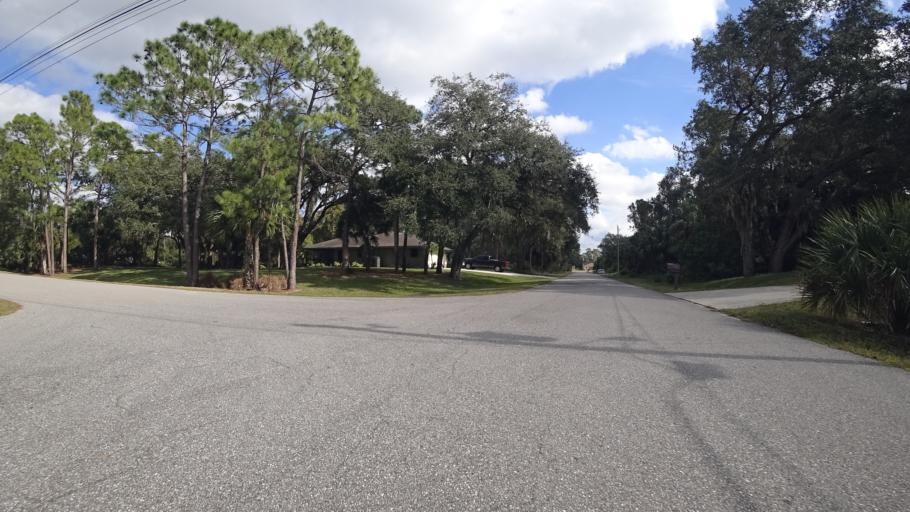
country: US
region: Florida
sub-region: Charlotte County
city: Port Charlotte
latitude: 27.0374
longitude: -82.1366
